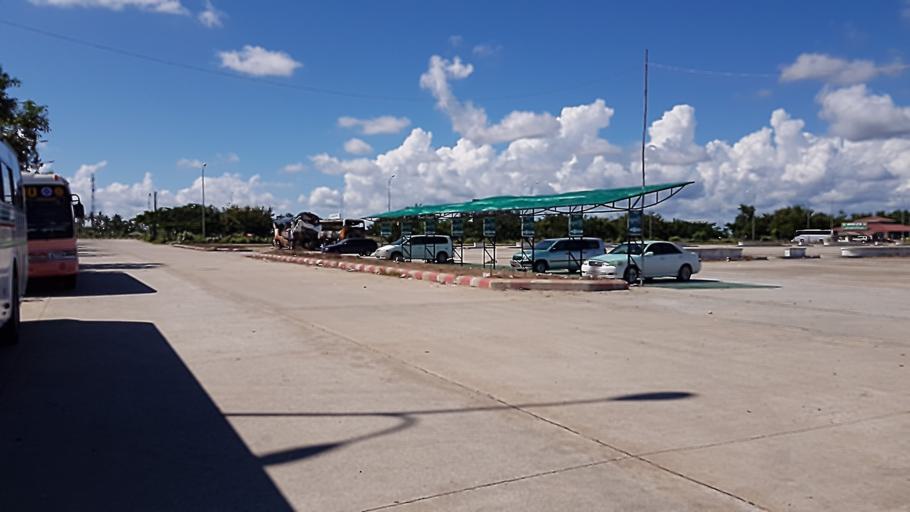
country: MM
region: Mandalay
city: Nay Pyi Taw
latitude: 19.6587
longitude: 96.0594
